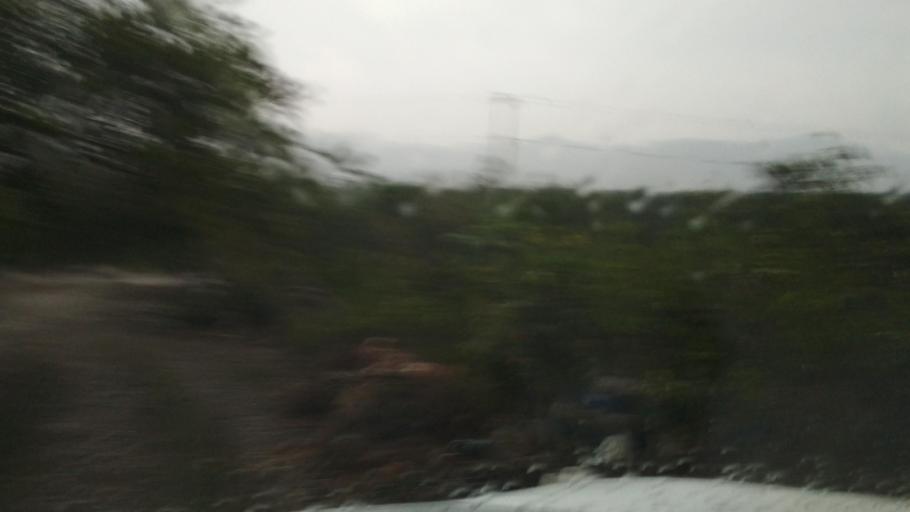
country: MM
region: Shan
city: Taunggyi
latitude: 20.3020
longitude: 97.3024
